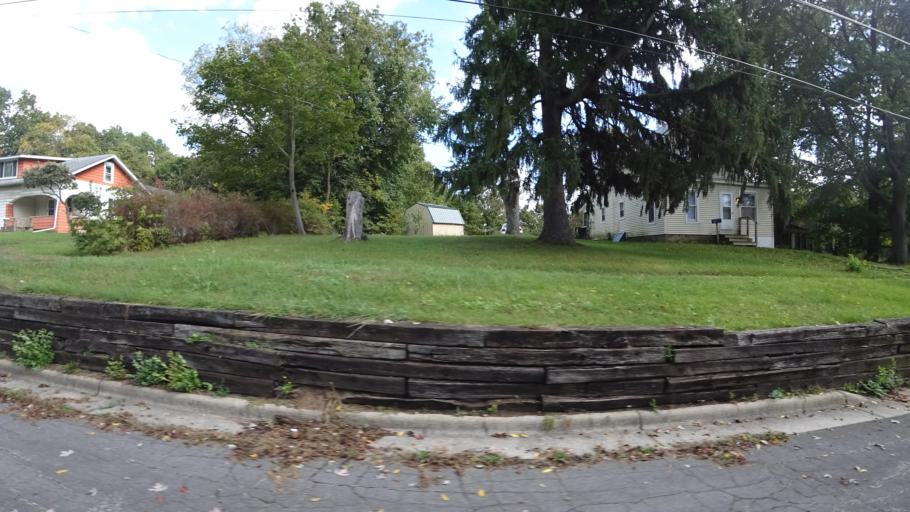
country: US
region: Michigan
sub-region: Saint Joseph County
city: Three Rivers
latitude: 41.9337
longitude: -85.6234
